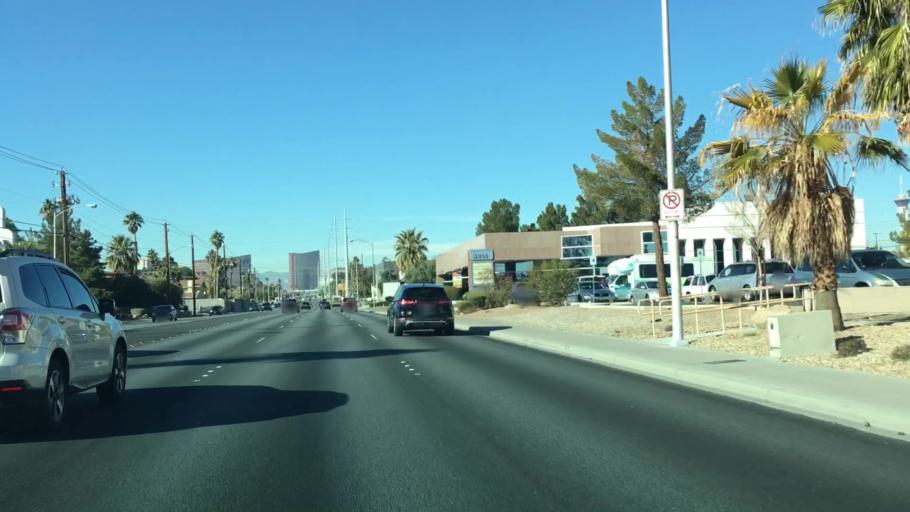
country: US
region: Nevada
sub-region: Clark County
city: Winchester
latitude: 36.1299
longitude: -115.1242
